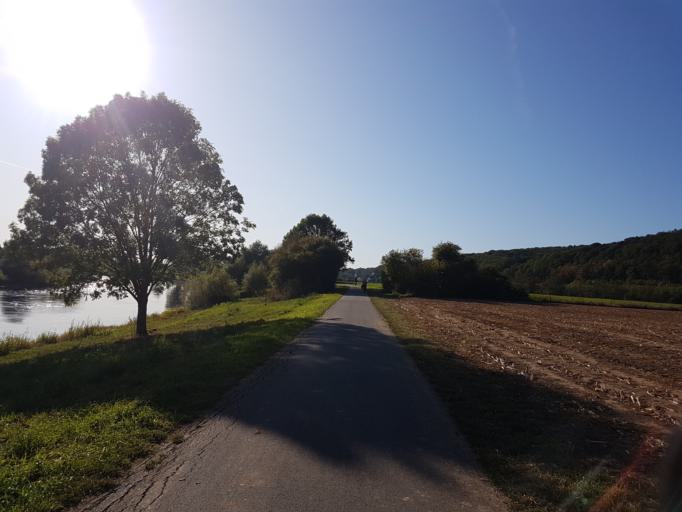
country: DE
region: North Rhine-Westphalia
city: Porta Westfalica
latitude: 52.2427
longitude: 8.8695
